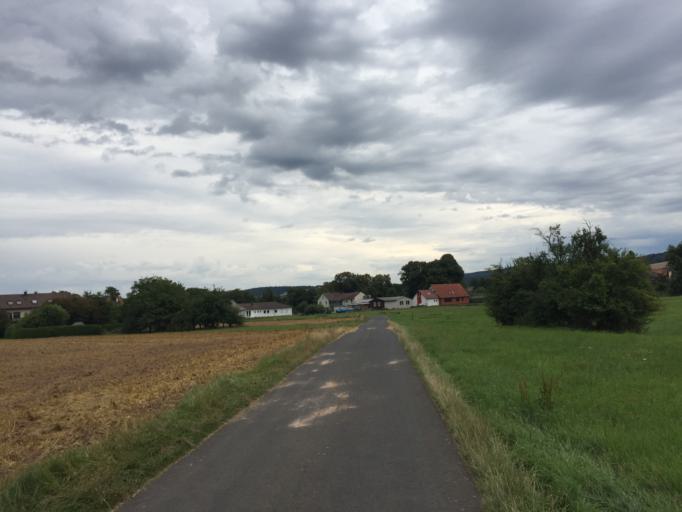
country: DE
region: Hesse
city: Breitenbach
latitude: 50.9213
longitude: 9.7565
